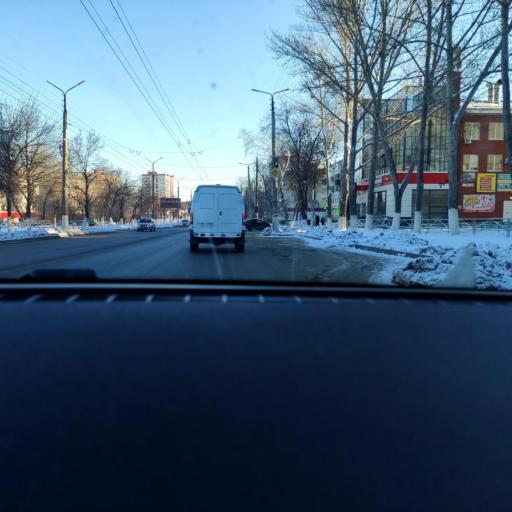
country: RU
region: Samara
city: Novokuybyshevsk
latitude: 53.0979
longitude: 49.9662
